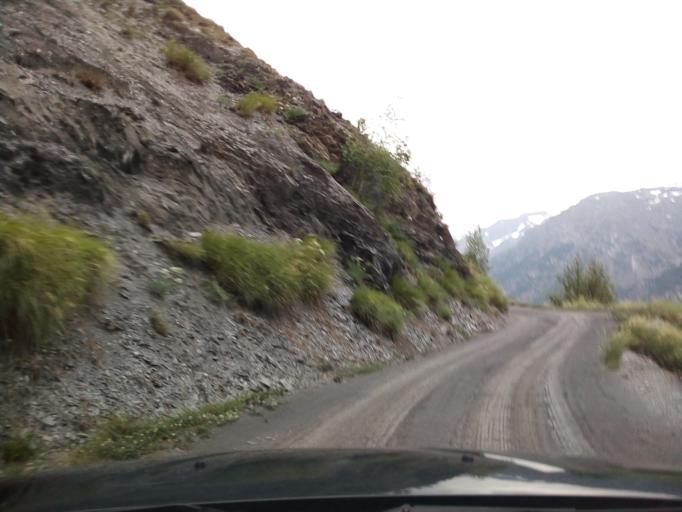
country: FR
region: Rhone-Alpes
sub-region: Departement de l'Isere
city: Mont-de-Lans
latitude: 45.0522
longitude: 6.1551
